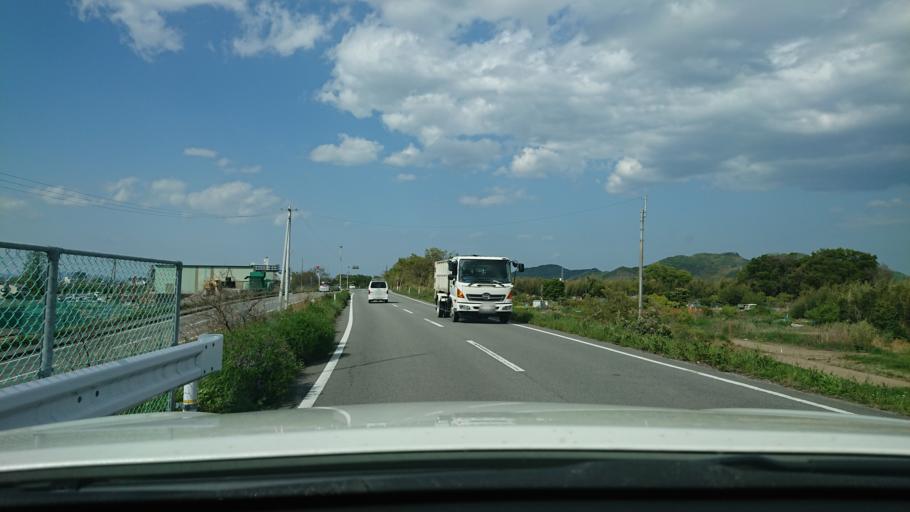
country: JP
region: Tokushima
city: Komatsushimacho
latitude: 34.0083
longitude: 134.5540
